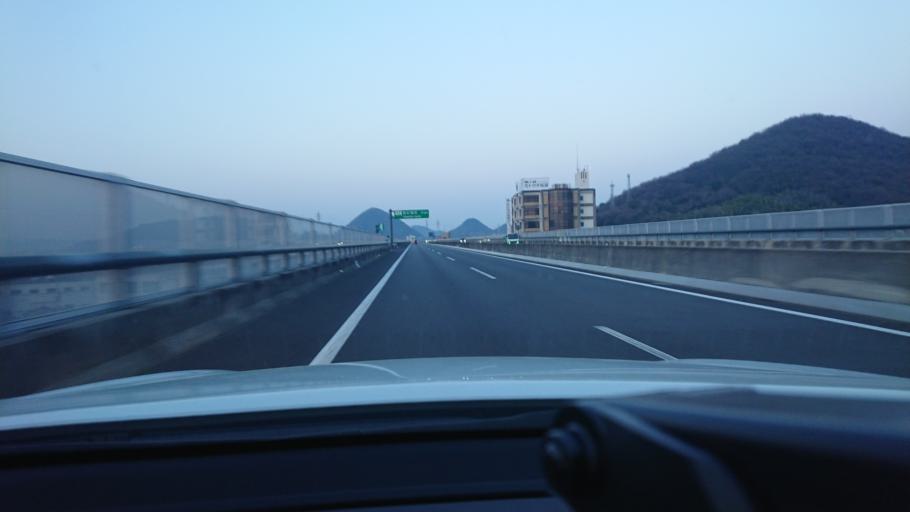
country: JP
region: Kagawa
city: Takamatsu-shi
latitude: 34.3117
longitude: 134.0255
